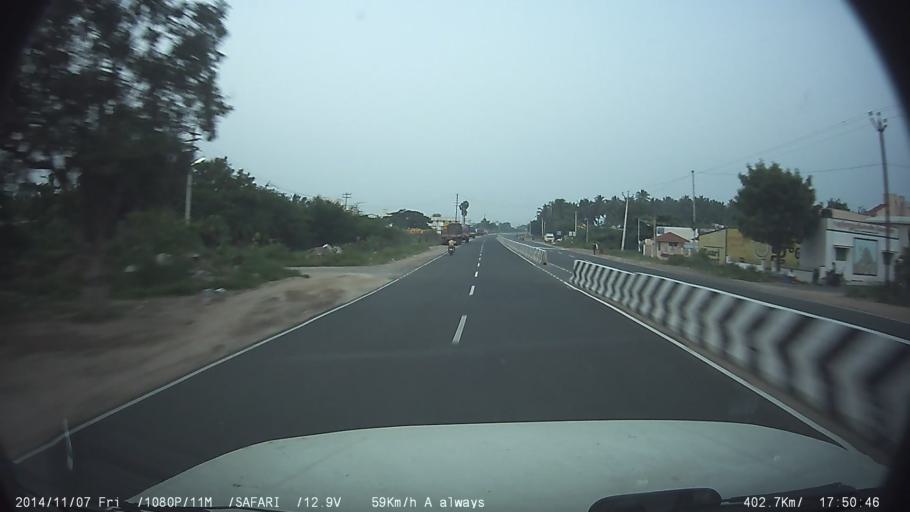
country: IN
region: Tamil Nadu
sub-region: Erode
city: Perundurai
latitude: 11.2838
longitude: 77.5910
